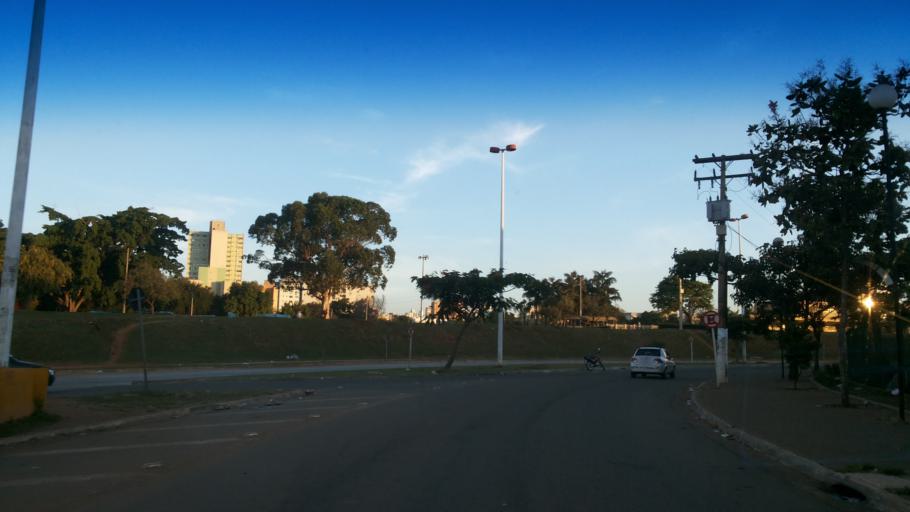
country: BR
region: Goias
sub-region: Goiania
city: Goiania
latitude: -16.6618
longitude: -49.2608
